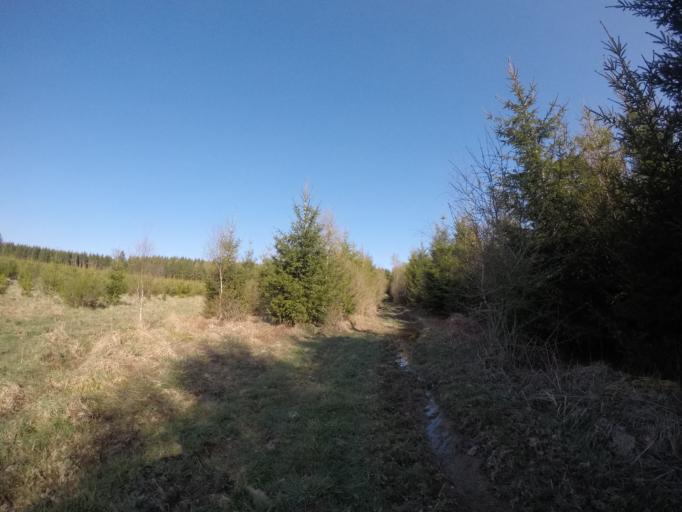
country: BE
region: Wallonia
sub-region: Province du Luxembourg
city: Leglise
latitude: 49.7919
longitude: 5.5861
